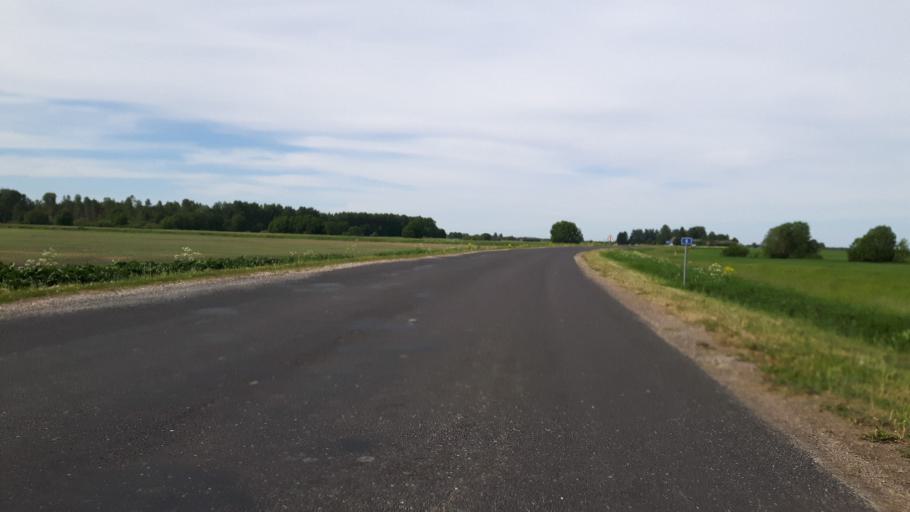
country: EE
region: Harju
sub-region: Raasiku vald
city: Arukula
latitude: 59.4233
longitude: 25.0774
